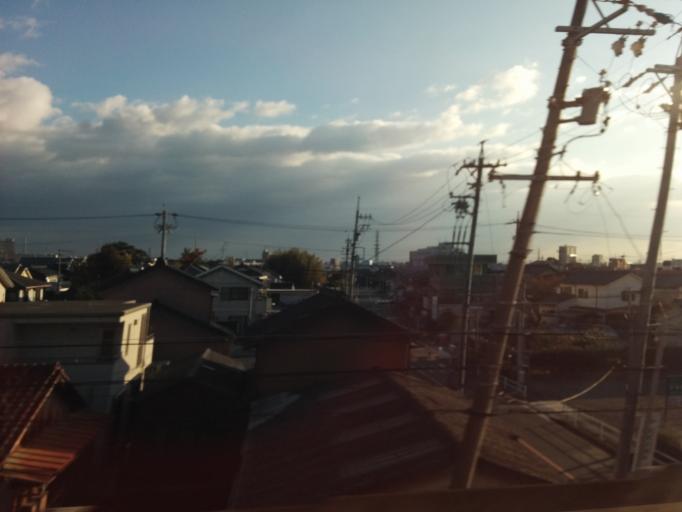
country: JP
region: Aichi
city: Obu
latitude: 35.0808
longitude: 136.9343
